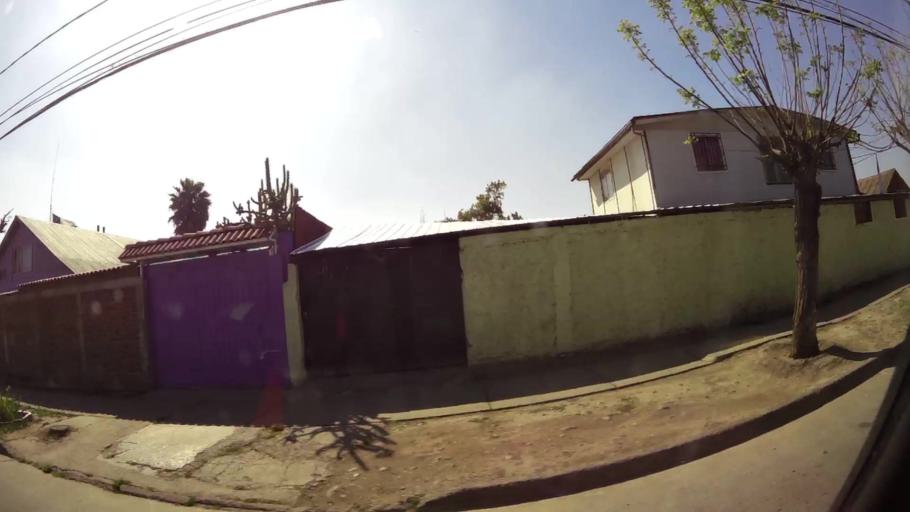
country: CL
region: Santiago Metropolitan
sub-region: Provincia de Santiago
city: Lo Prado
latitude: -33.5100
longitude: -70.7716
